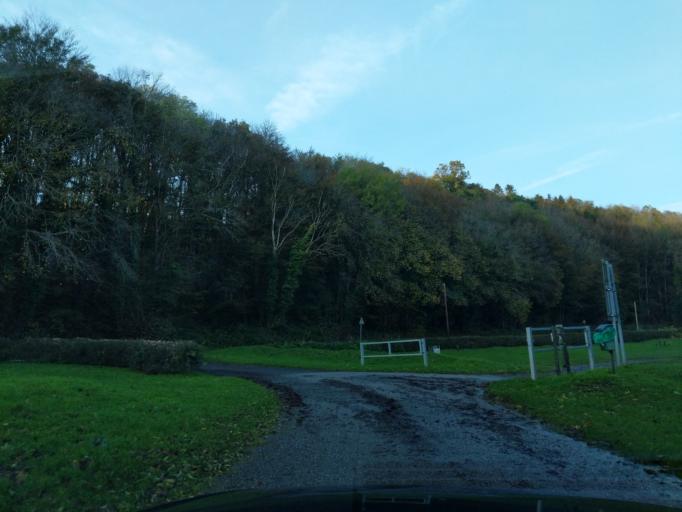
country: GB
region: Scotland
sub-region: Dumfries and Galloway
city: Kirkcudbright
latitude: 54.8148
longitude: -4.0916
